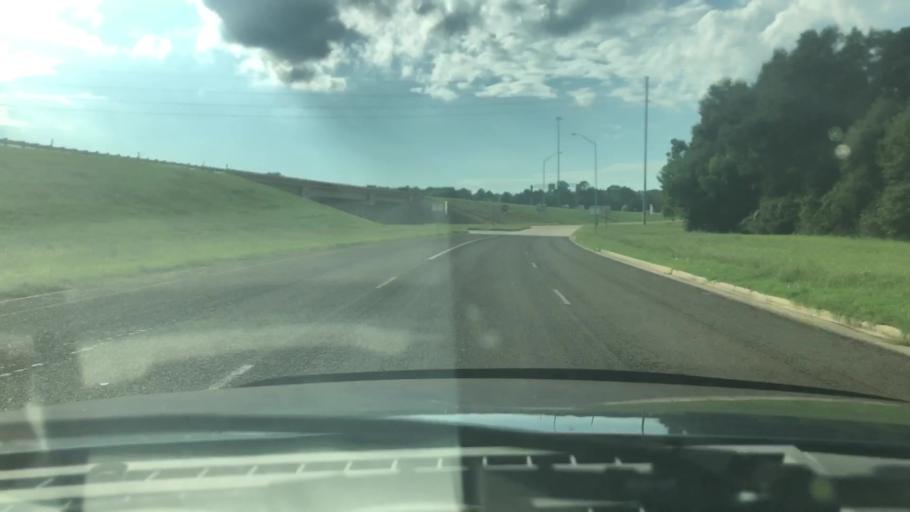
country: US
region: Texas
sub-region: Bowie County
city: Wake Village
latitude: 33.3868
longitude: -94.0906
